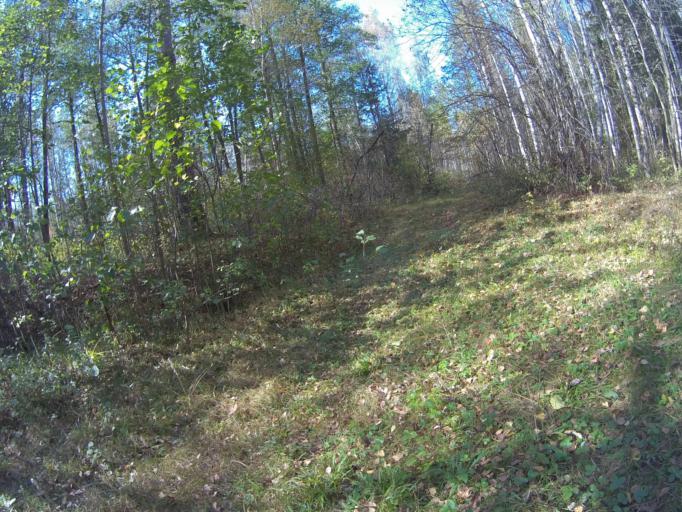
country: RU
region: Vladimir
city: Sobinka
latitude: 55.9333
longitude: 40.0870
